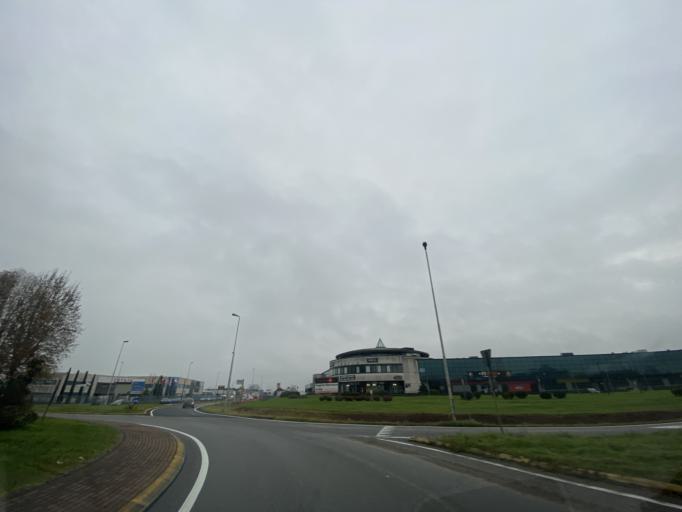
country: IT
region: Lombardy
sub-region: Citta metropolitana di Milano
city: Cusago
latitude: 45.4445
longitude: 9.0399
